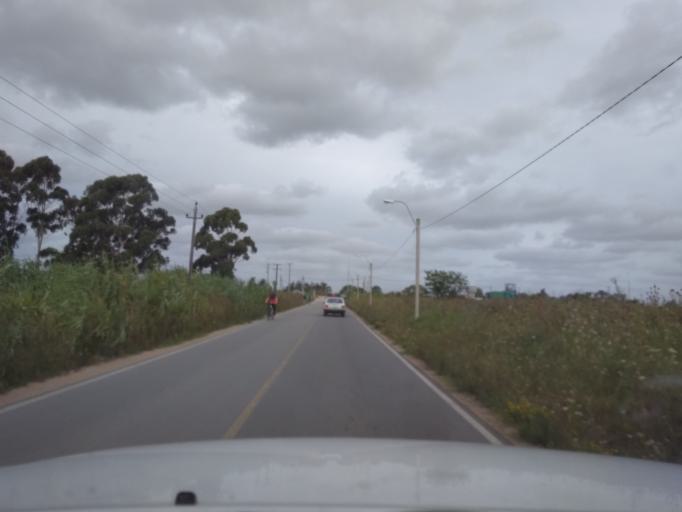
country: UY
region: Canelones
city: Colonia Nicolich
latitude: -34.7863
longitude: -56.0028
